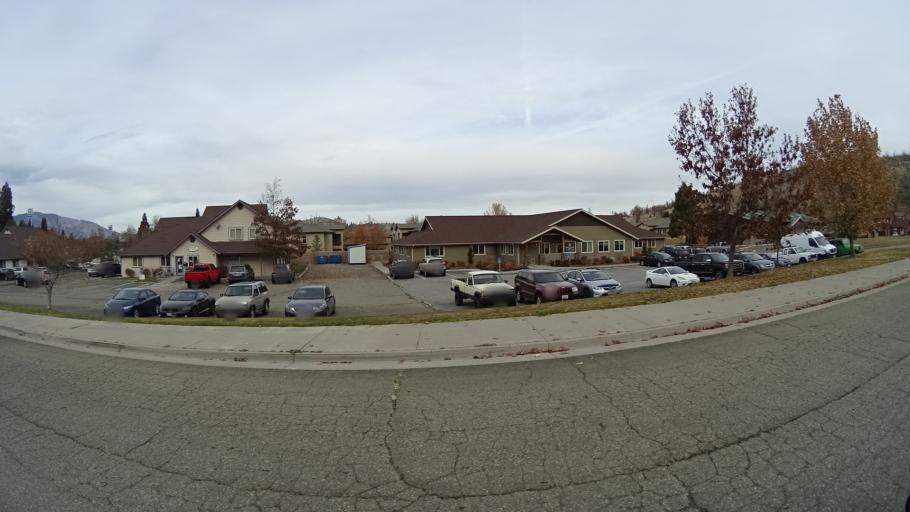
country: US
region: California
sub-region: Siskiyou County
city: Weed
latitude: 41.4208
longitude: -122.3818
